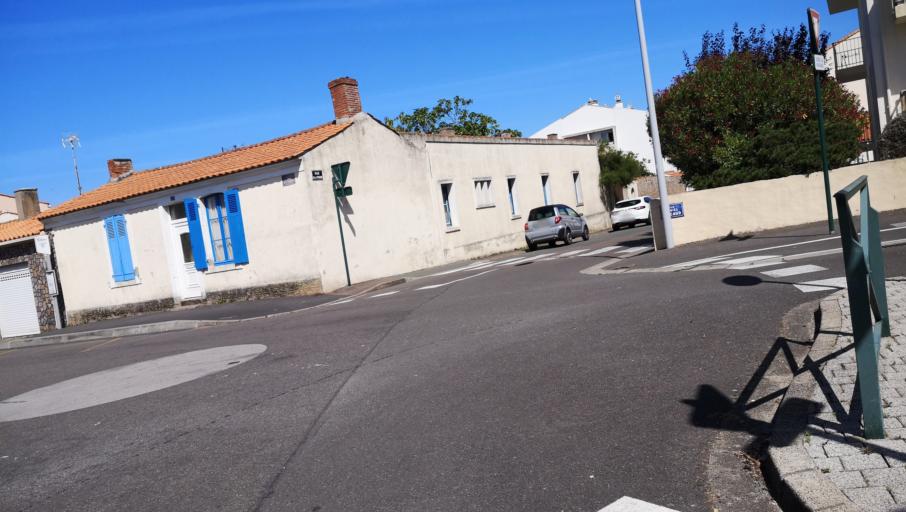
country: FR
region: Pays de la Loire
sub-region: Departement de la Vendee
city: Les Sables-d'Olonne
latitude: 46.4986
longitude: -1.7723
